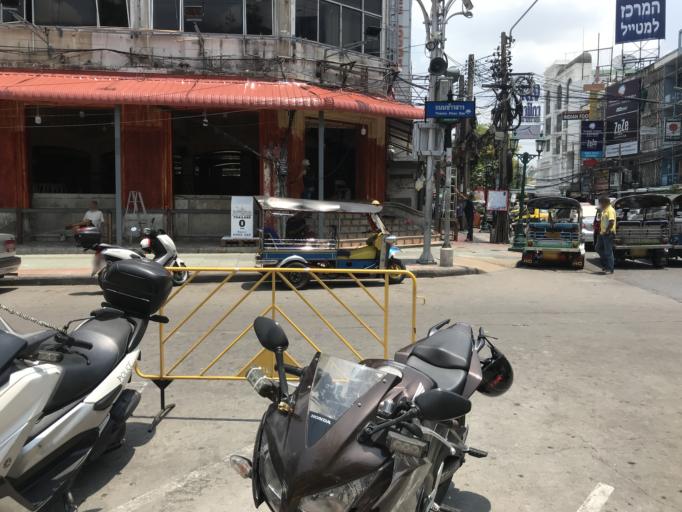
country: TH
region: Bangkok
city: Phra Nakhon
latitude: 13.7597
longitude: 100.4957
